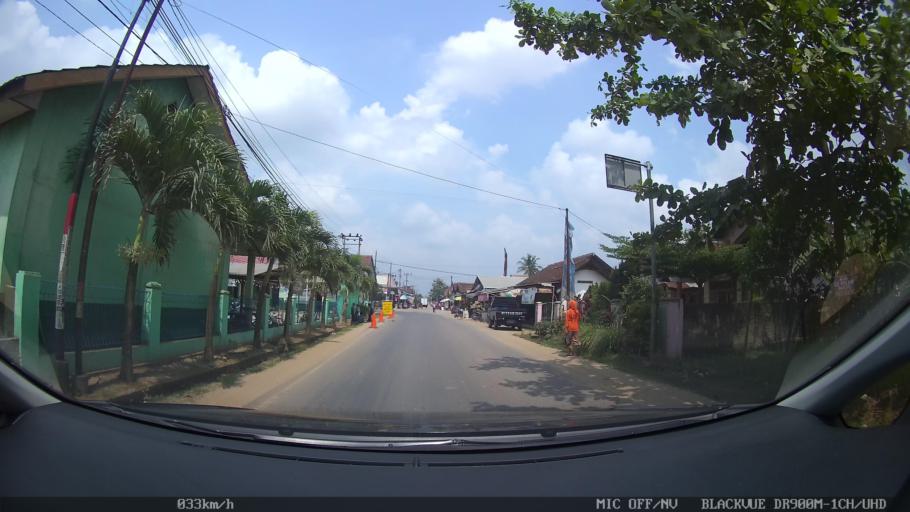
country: ID
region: Lampung
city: Pringsewu
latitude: -5.3875
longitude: 104.9614
